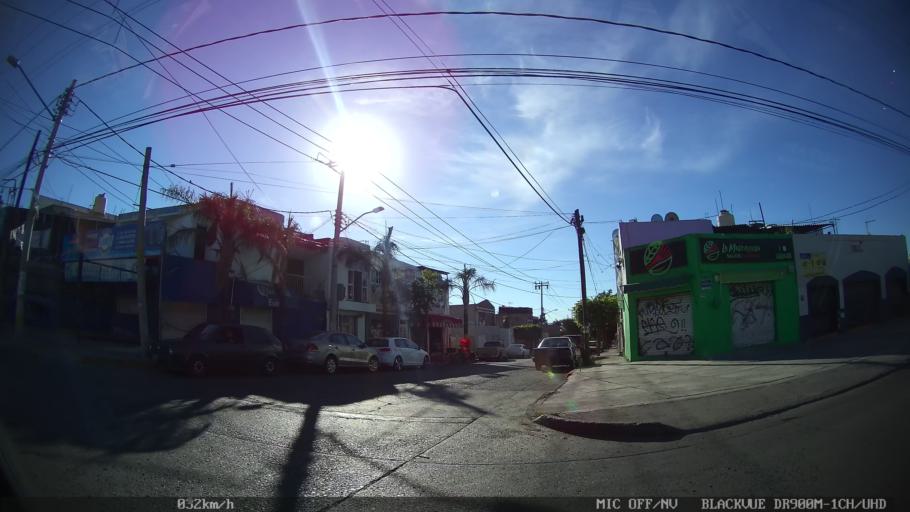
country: MX
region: Jalisco
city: Tlaquepaque
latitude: 20.6964
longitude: -103.2943
